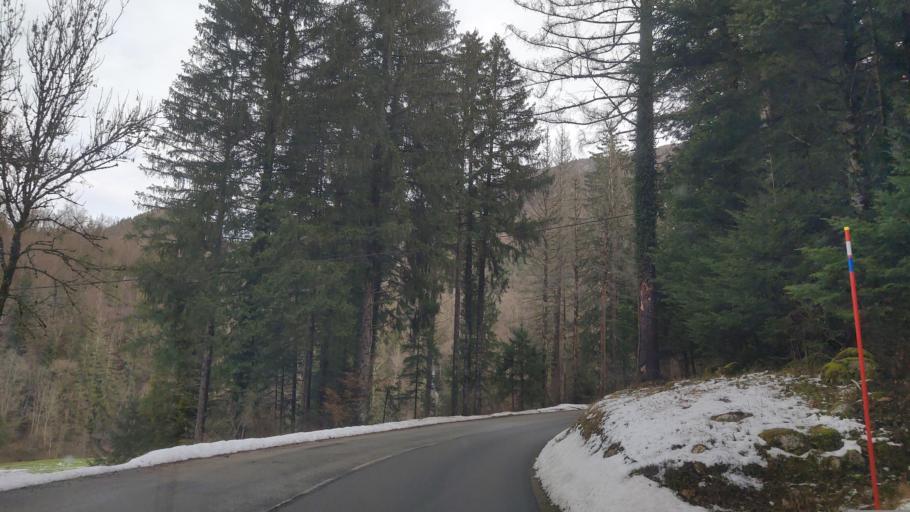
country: FR
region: Rhone-Alpes
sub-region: Departement de la Haute-Savoie
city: Doussard
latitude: 45.6739
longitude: 6.1399
